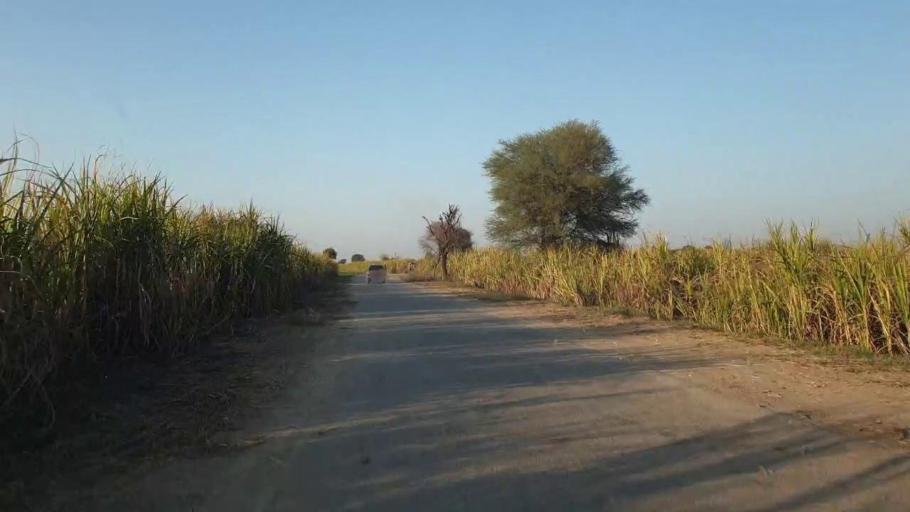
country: PK
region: Sindh
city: Chambar
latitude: 25.3609
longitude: 68.7401
